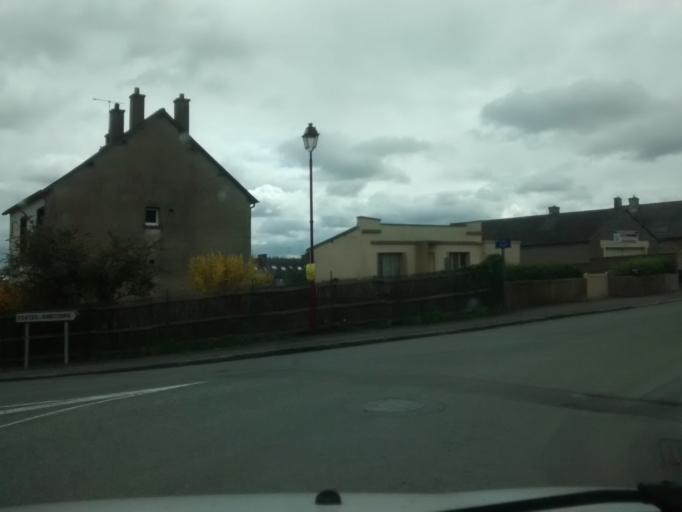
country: FR
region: Brittany
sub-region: Departement d'Ille-et-Vilaine
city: Saint-Pere
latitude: 48.5602
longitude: -1.9326
